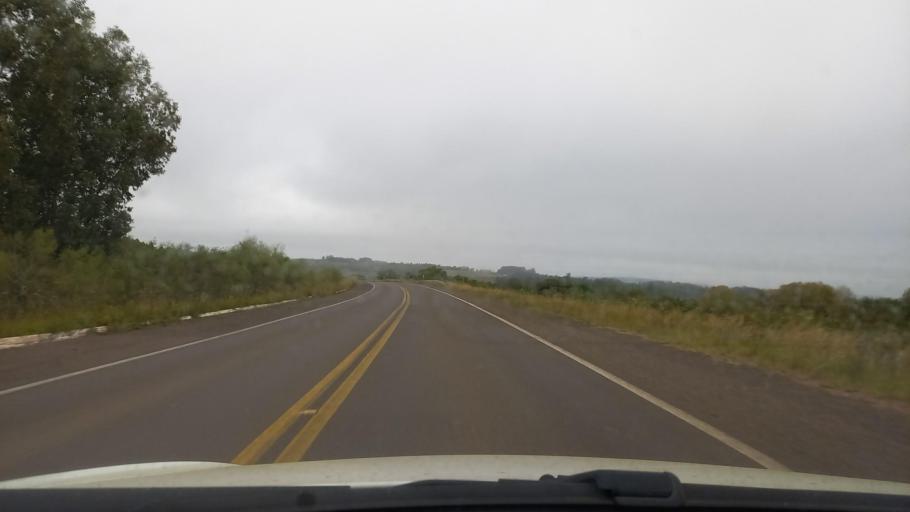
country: BR
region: Rio Grande do Sul
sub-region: Cacequi
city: Cacequi
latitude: -30.1035
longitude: -54.6331
